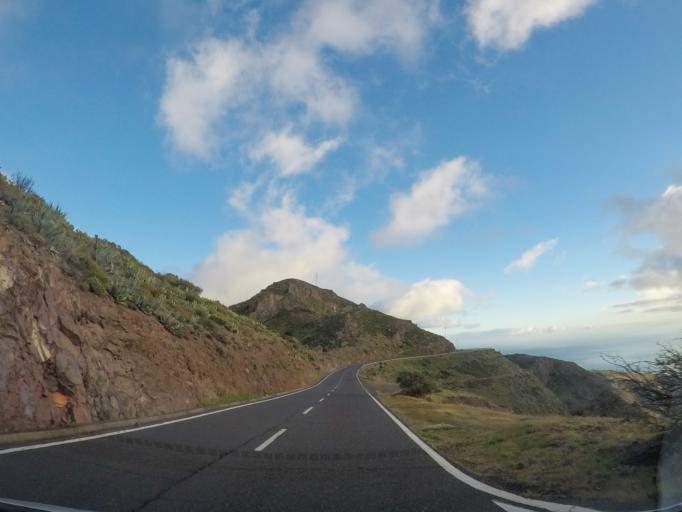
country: ES
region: Canary Islands
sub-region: Provincia de Santa Cruz de Tenerife
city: Alajero
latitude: 28.0818
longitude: -17.2445
